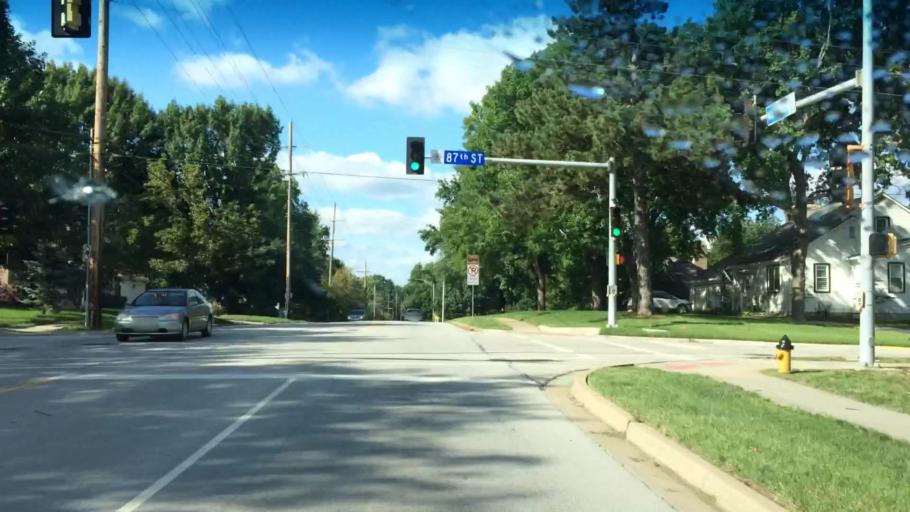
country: US
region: Kansas
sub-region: Johnson County
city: Overland Park
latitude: 38.9711
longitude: -94.6490
